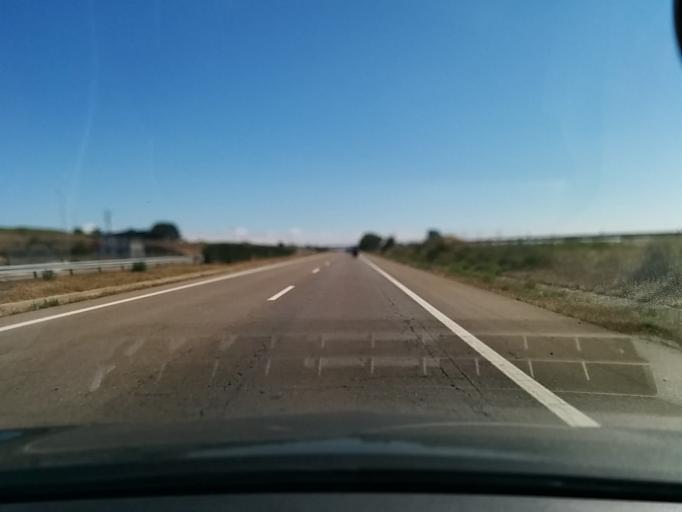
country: ES
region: Aragon
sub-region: Provincia de Huesca
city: Almudebar
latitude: 42.0181
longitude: -0.6136
